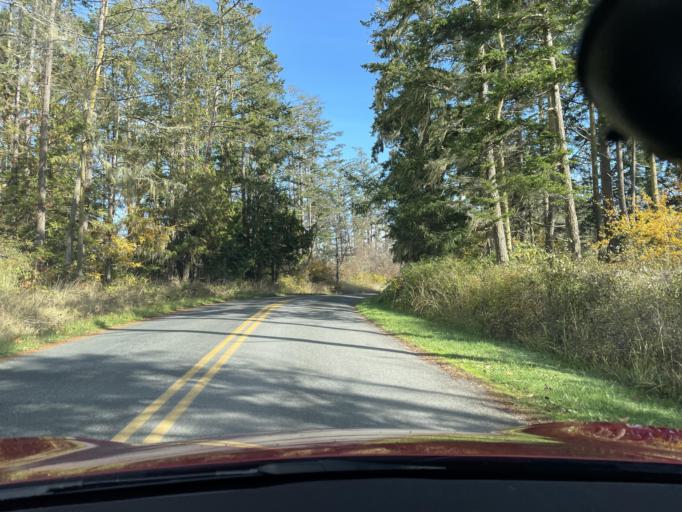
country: US
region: Washington
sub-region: San Juan County
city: Friday Harbor
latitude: 48.5036
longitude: -123.0226
